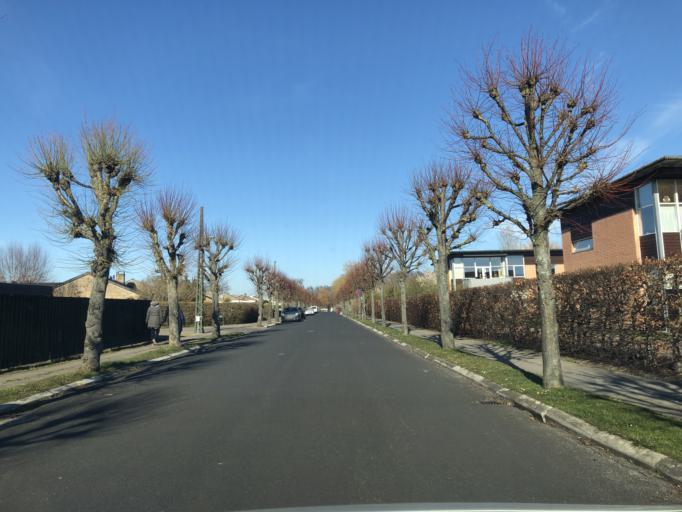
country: DK
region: Capital Region
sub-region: Dragor Kommune
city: Dragor
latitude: 55.5865
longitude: 12.6592
